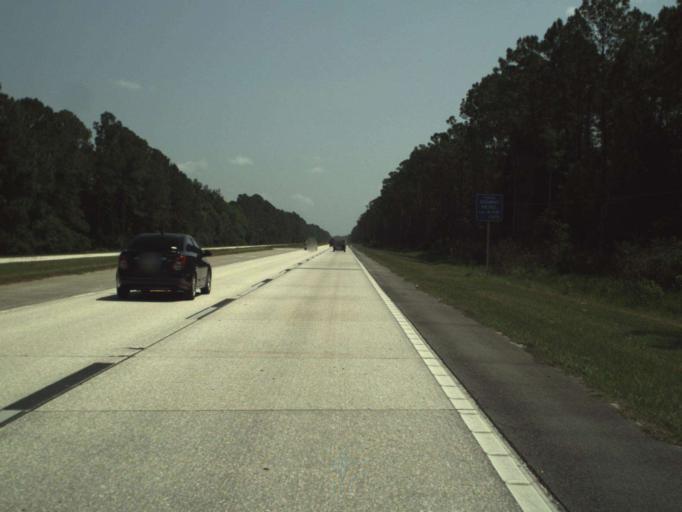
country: US
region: Florida
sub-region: Volusia County
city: North DeLand
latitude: 29.0772
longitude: -81.2452
